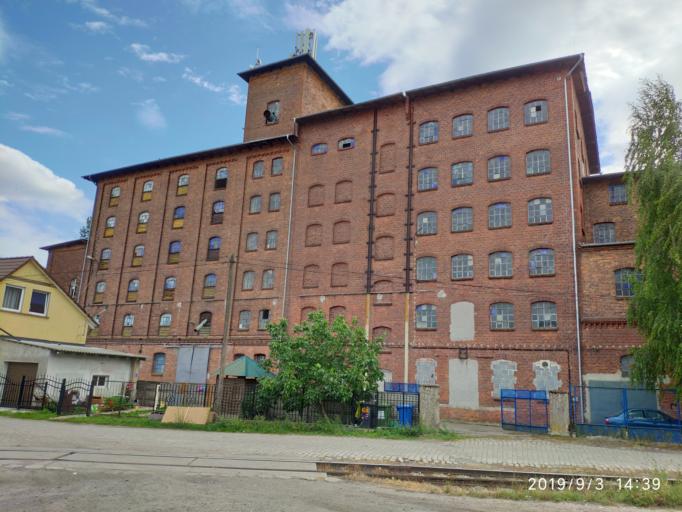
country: PL
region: Lubusz
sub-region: Powiat nowosolski
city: Nowa Sol
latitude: 51.7927
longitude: 15.7171
